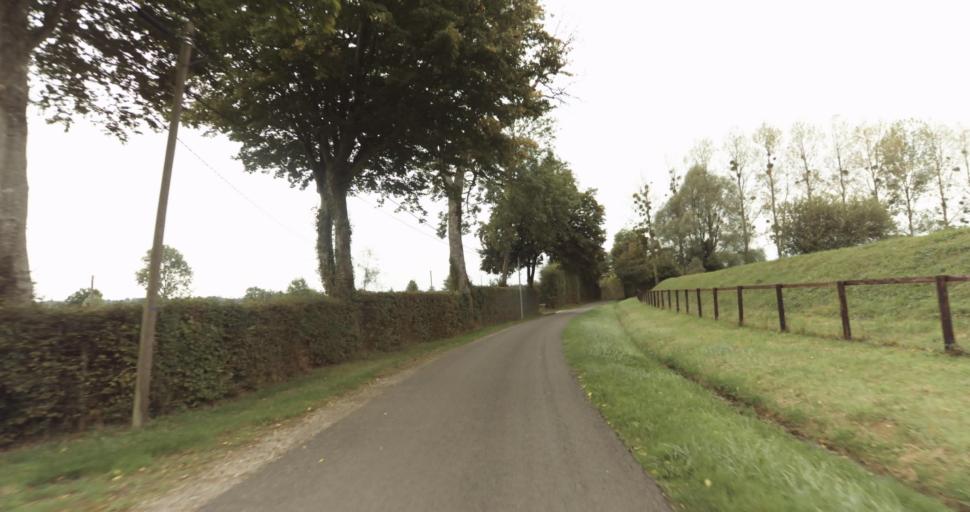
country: FR
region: Lower Normandy
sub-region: Departement de l'Orne
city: Gace
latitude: 48.7405
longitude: 0.2933
